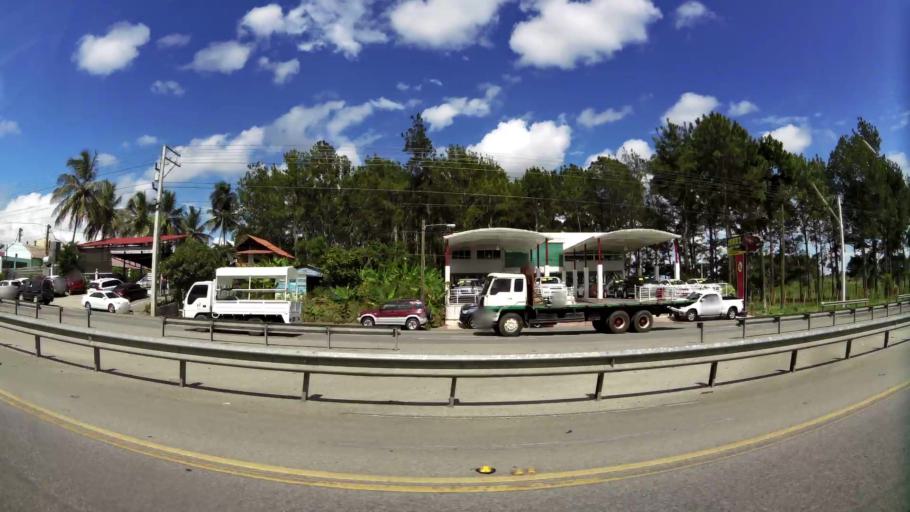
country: DO
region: La Vega
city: Rio Verde Arriba
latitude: 19.3282
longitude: -70.5916
